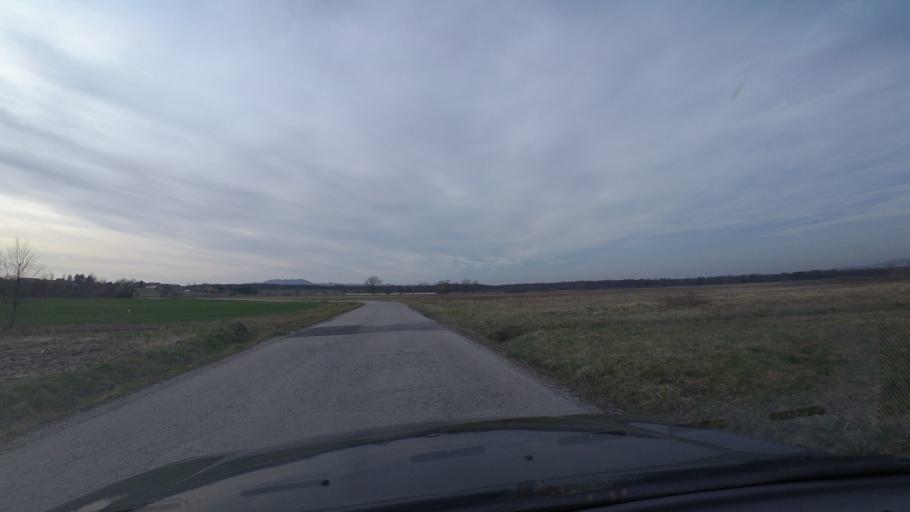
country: HR
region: Grad Zagreb
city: Horvati
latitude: 45.6903
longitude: 15.8486
